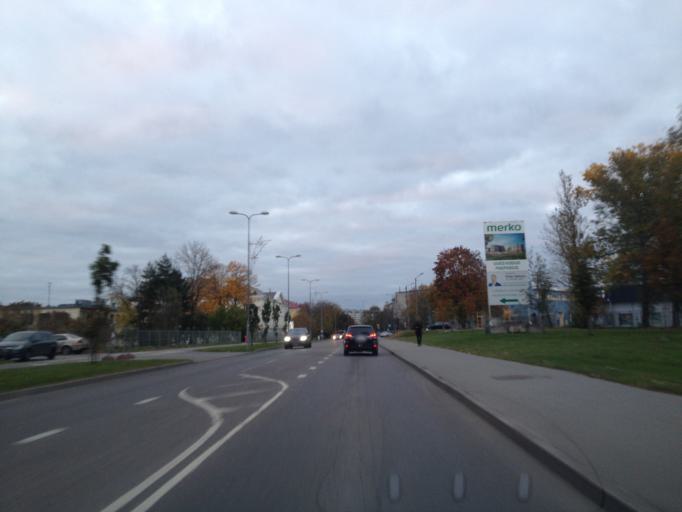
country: EE
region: Harju
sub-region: Tallinna linn
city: Tallinn
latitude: 59.4309
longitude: 24.8087
